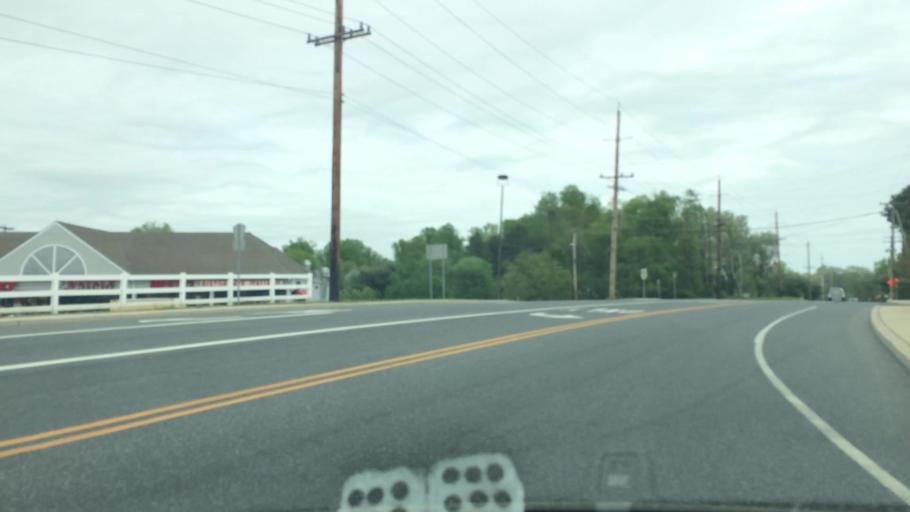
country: US
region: New Jersey
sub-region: Gloucester County
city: Turnersville
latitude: 39.7649
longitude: -75.0855
